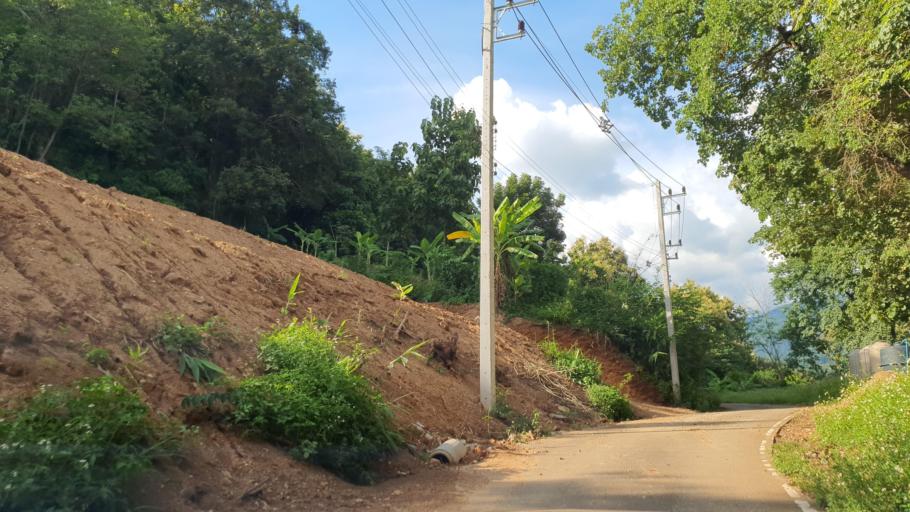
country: TH
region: Chiang Mai
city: Hang Dong
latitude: 18.7612
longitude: 98.8688
